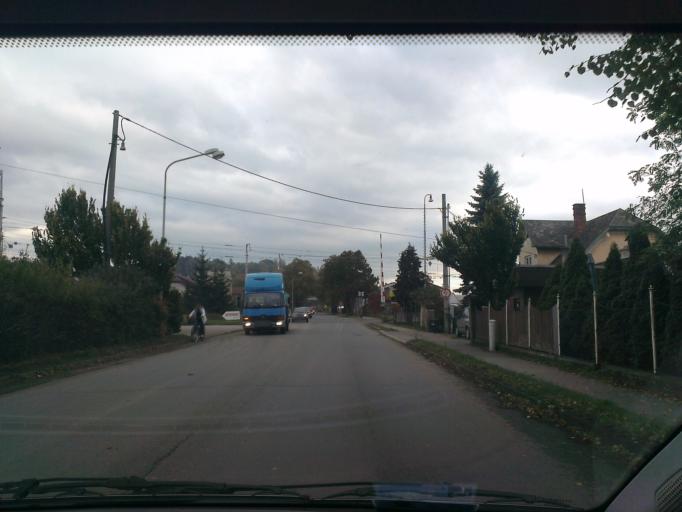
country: CZ
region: Zlin
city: Valasske Mezirici
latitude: 49.4816
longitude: 17.9628
